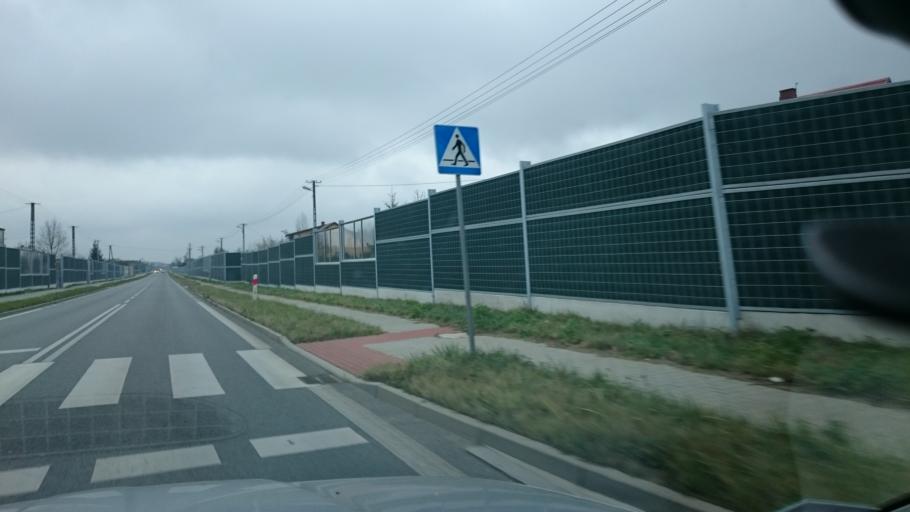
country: PL
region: Swietokrzyskie
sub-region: Powiat konecki
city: Konskie
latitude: 51.1673
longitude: 20.3782
